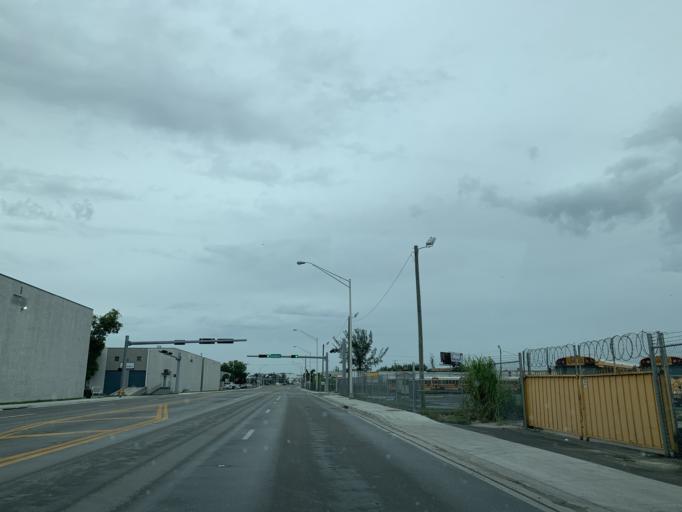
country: US
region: Florida
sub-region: Miami-Dade County
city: Hialeah Gardens
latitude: 25.8625
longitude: -80.3386
